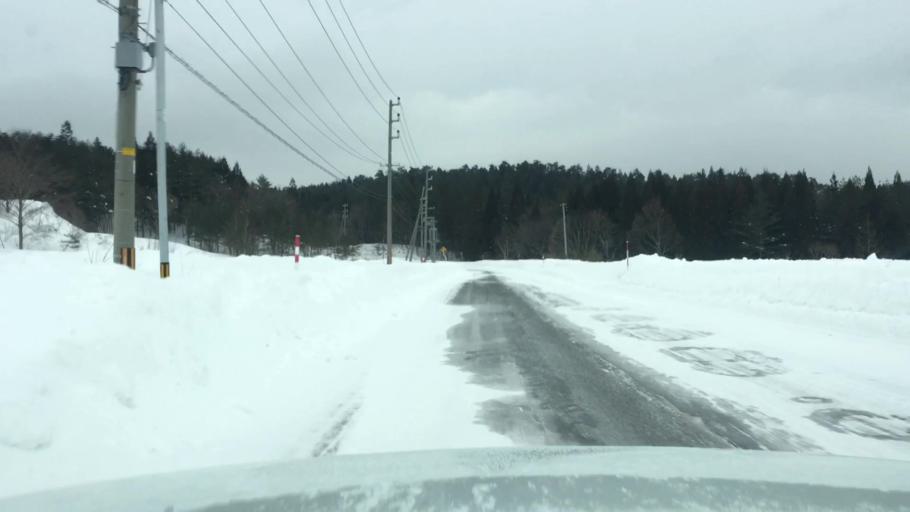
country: JP
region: Akita
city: Hanawa
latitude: 39.9930
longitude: 140.9956
